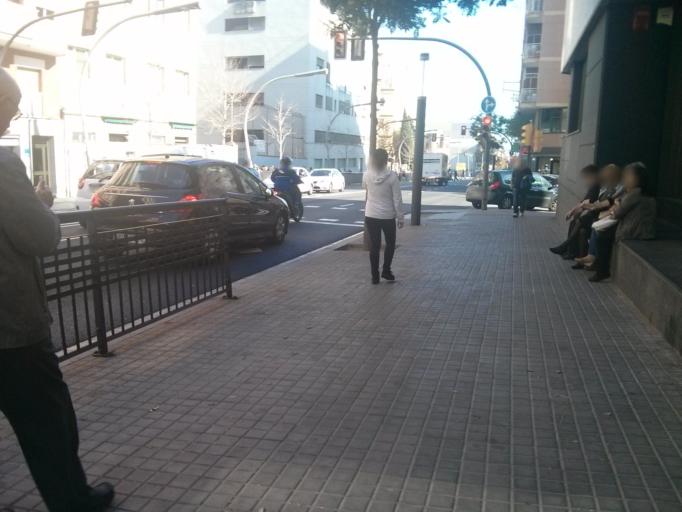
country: ES
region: Catalonia
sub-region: Provincia de Barcelona
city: les Corts
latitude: 41.3755
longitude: 2.1154
